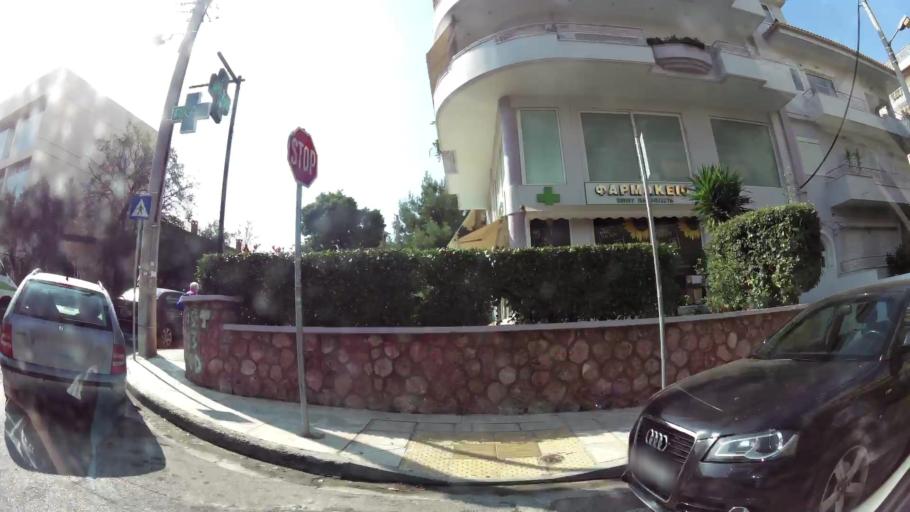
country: GR
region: Attica
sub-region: Nomarchia Athinas
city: Cholargos
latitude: 37.9989
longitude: 23.8003
